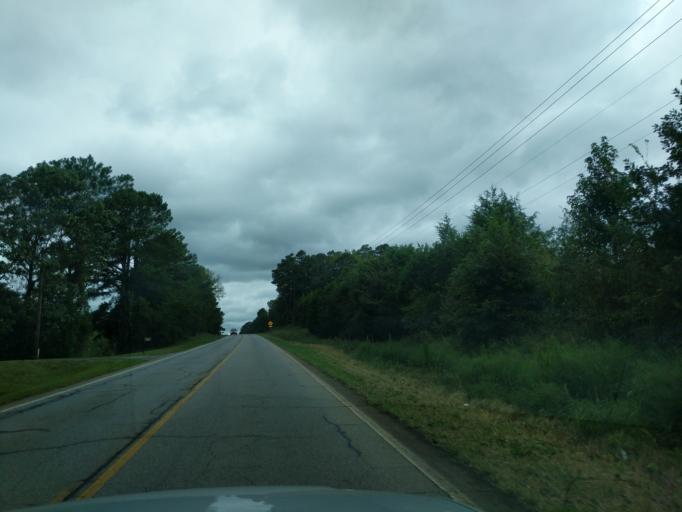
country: US
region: Georgia
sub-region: Wilkes County
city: Washington
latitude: 33.6894
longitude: -82.6632
